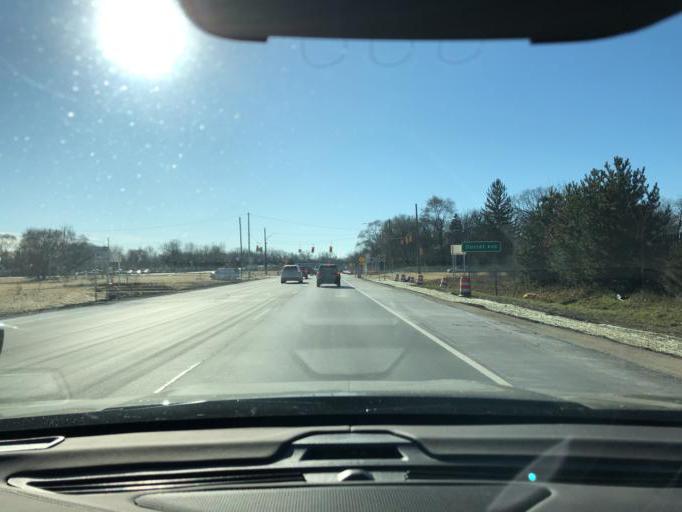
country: US
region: Michigan
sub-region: Washtenaw County
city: Ypsilanti
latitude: 42.2365
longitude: -83.5744
